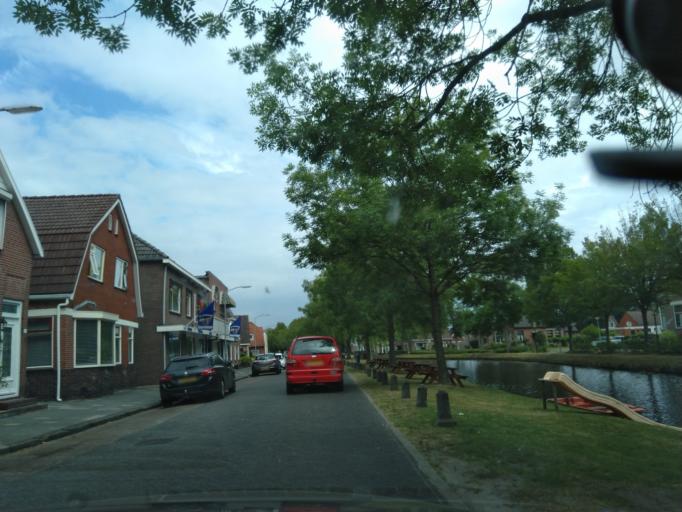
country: NL
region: Groningen
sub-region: Gemeente Pekela
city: Oude Pekela
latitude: 53.1005
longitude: 7.0015
